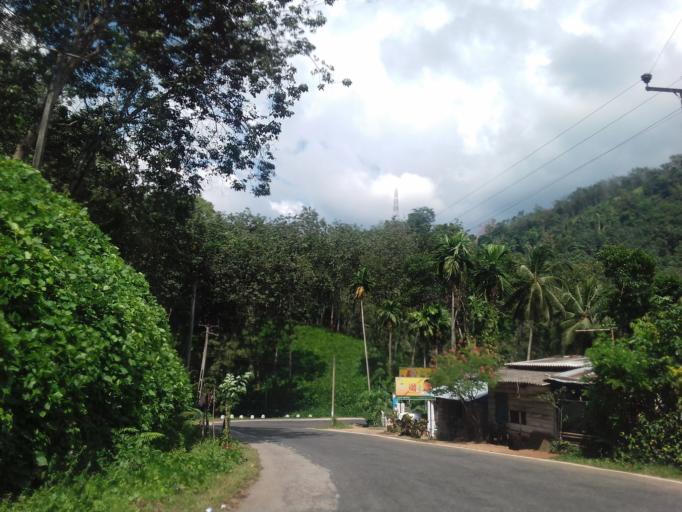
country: LK
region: Central
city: Hatton
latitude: 6.9968
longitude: 80.3526
